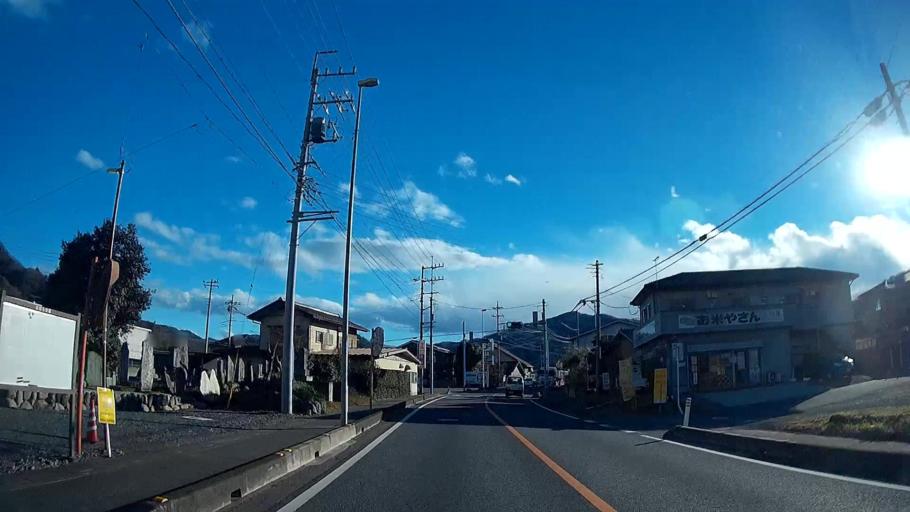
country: JP
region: Saitama
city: Yorii
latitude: 36.0902
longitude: 139.1133
